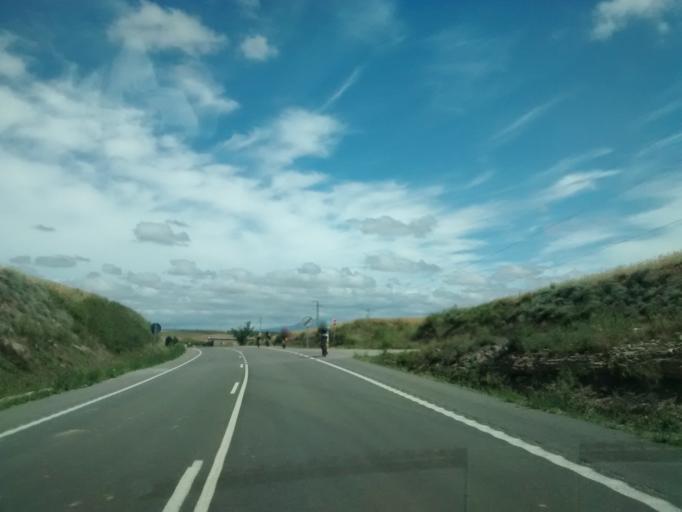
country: ES
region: La Rioja
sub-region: Provincia de La Rioja
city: Clavijo
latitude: 42.3691
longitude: -2.3882
